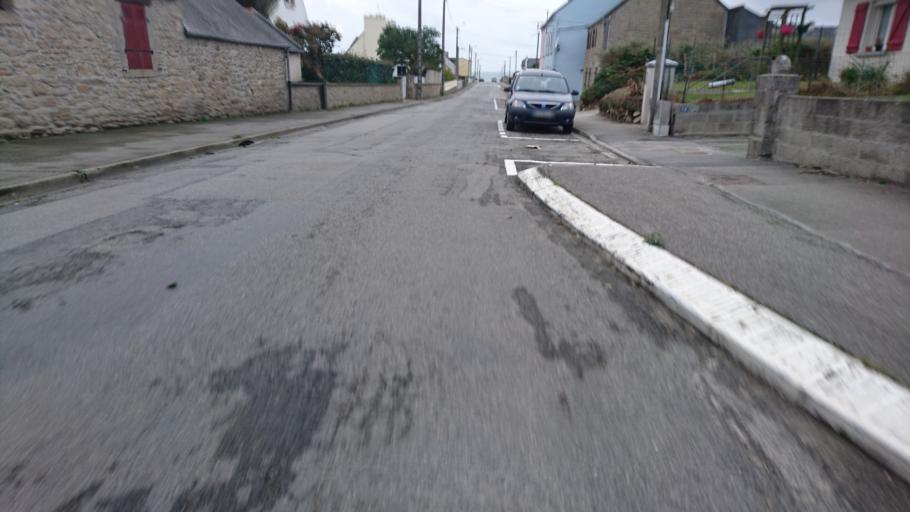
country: FR
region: Brittany
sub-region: Departement du Finistere
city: Lampaul-Plouarzel
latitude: 48.4484
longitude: -4.7679
